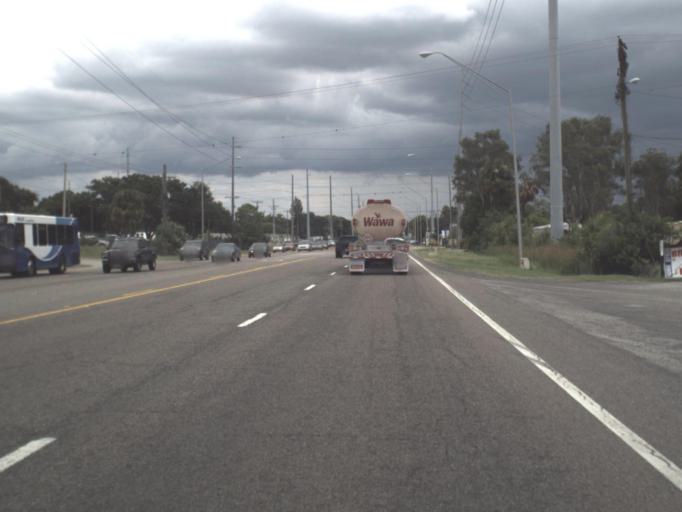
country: US
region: Florida
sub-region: Hillsborough County
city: Palm River-Clair Mel
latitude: 27.9230
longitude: -82.4115
